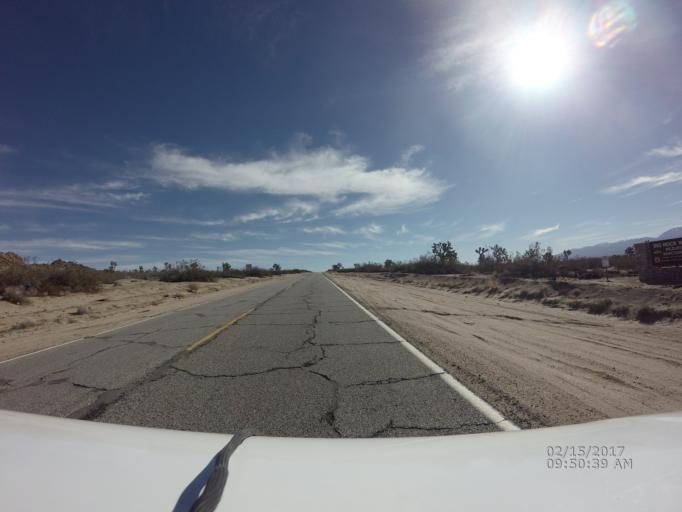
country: US
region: California
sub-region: Los Angeles County
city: Lake Los Angeles
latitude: 34.6167
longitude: -117.9175
